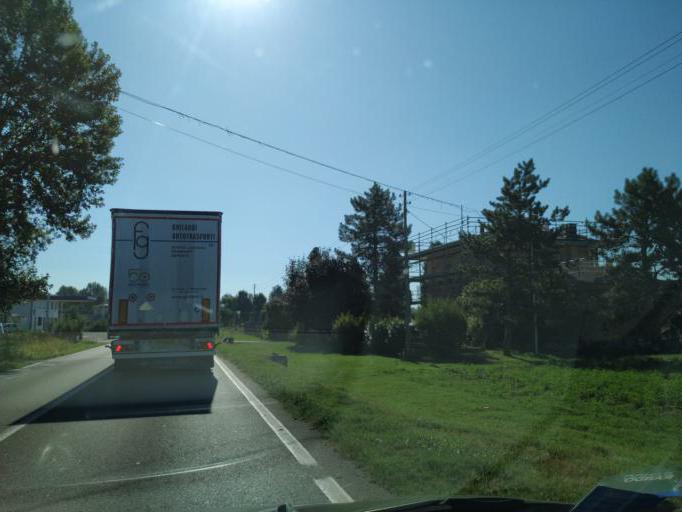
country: IT
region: Emilia-Romagna
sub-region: Provincia di Bologna
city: San Giovanni in Persiceto
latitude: 44.6469
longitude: 11.1663
